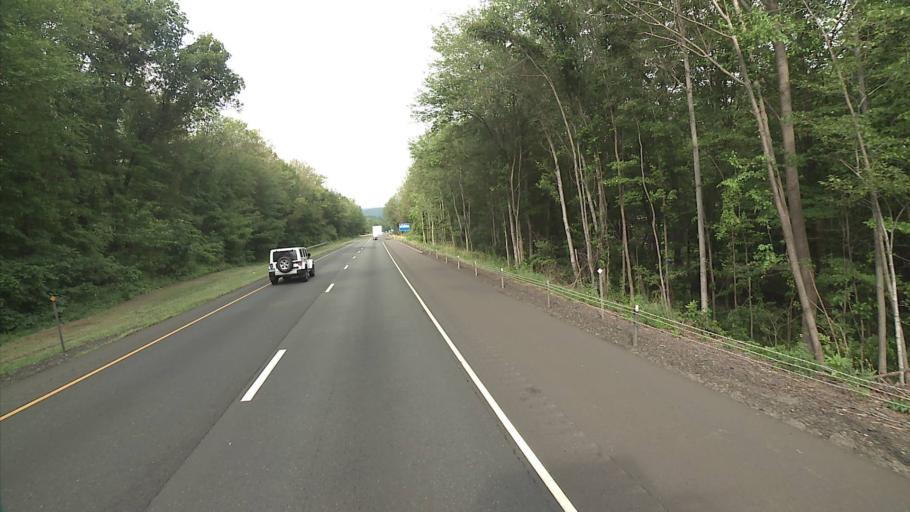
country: US
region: Connecticut
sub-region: New Haven County
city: Southbury
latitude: 41.4823
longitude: -73.1942
